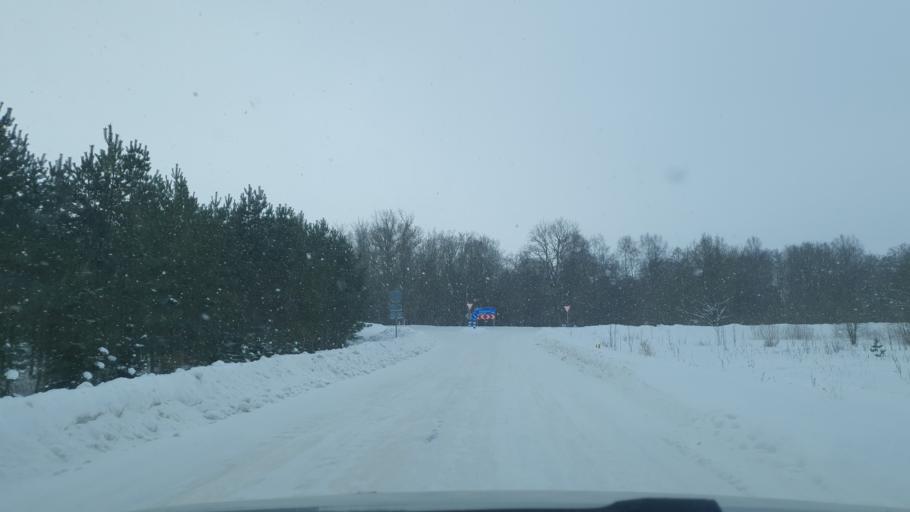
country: EE
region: Harju
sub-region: Kuusalu vald
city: Kuusalu
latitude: 59.4816
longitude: 25.3417
